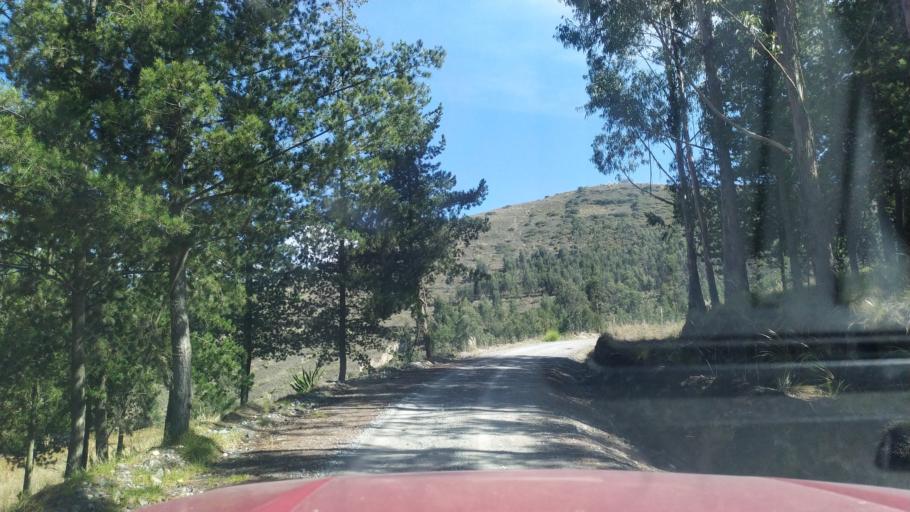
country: EC
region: Chimborazo
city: Riobamba
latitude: -1.6774
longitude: -78.6948
